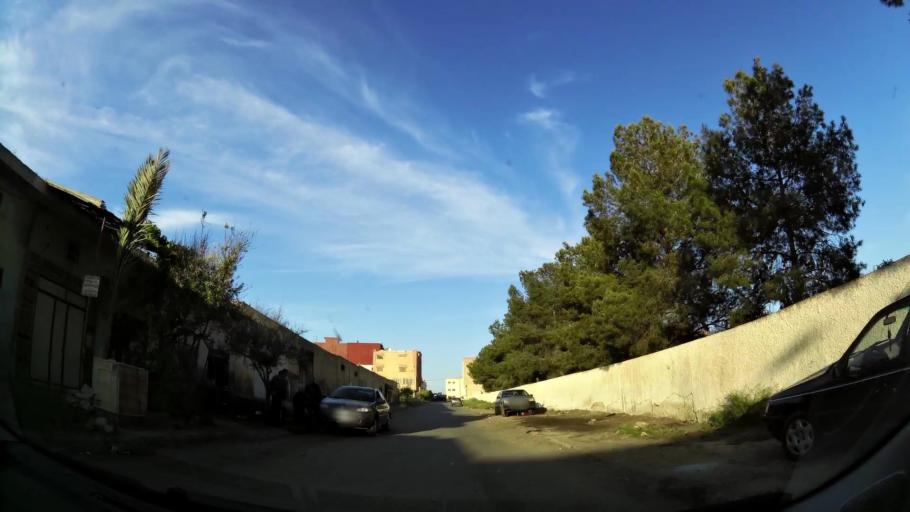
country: MA
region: Oriental
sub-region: Oujda-Angad
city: Oujda
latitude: 34.6999
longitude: -1.9180
